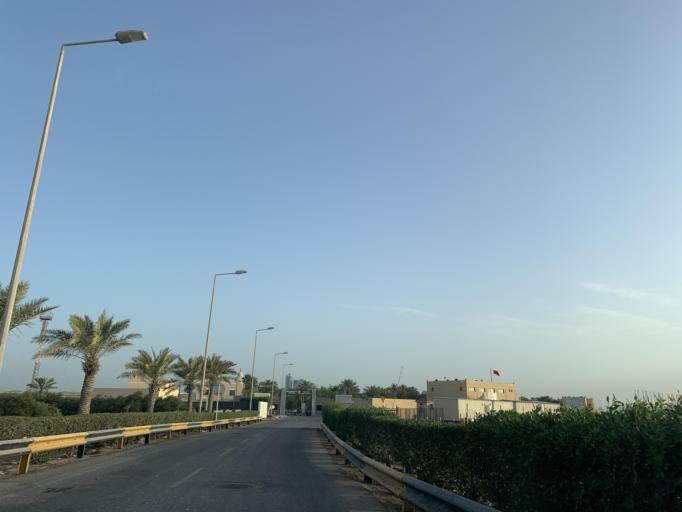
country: BH
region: Manama
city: Manama
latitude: 26.1881
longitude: 50.5855
